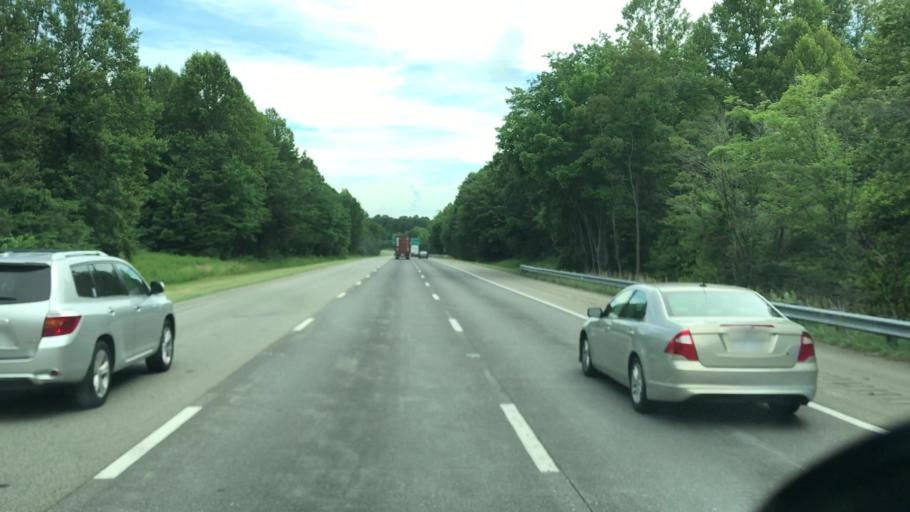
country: US
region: North Carolina
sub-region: Surry County
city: Dobson
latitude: 36.5021
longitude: -80.7424
